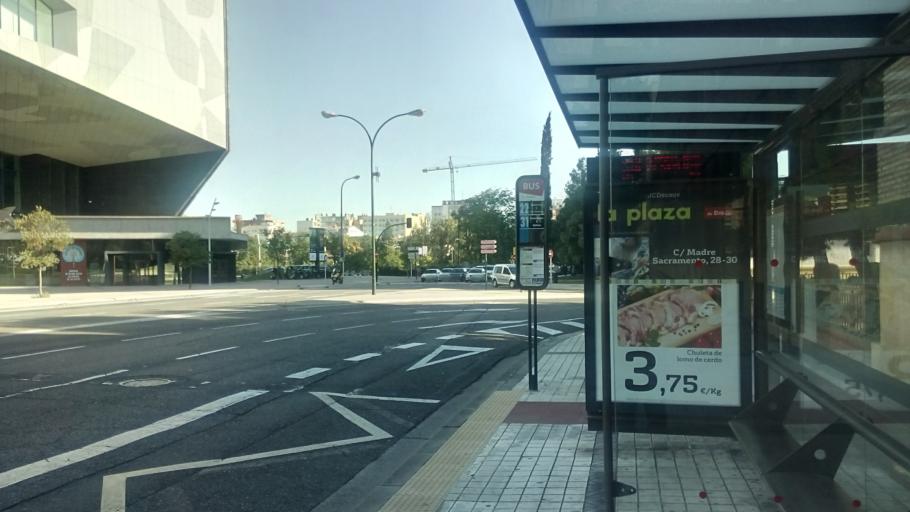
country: ES
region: Aragon
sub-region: Provincia de Zaragoza
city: Almozara
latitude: 41.6517
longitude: -0.8934
